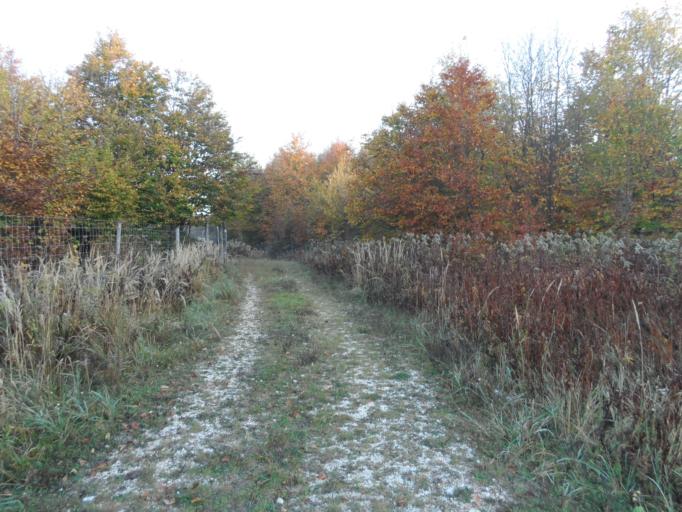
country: HU
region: Veszprem
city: Herend
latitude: 47.1900
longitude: 17.6941
